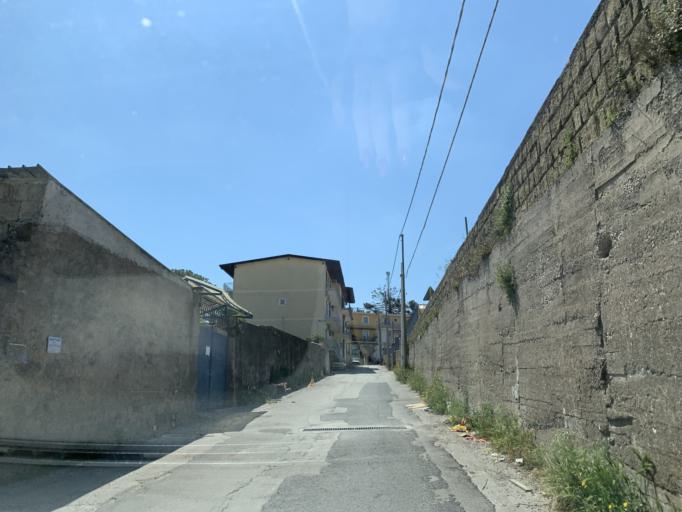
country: IT
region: Campania
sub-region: Provincia di Napoli
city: Napoli
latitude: 40.8782
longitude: 14.2364
